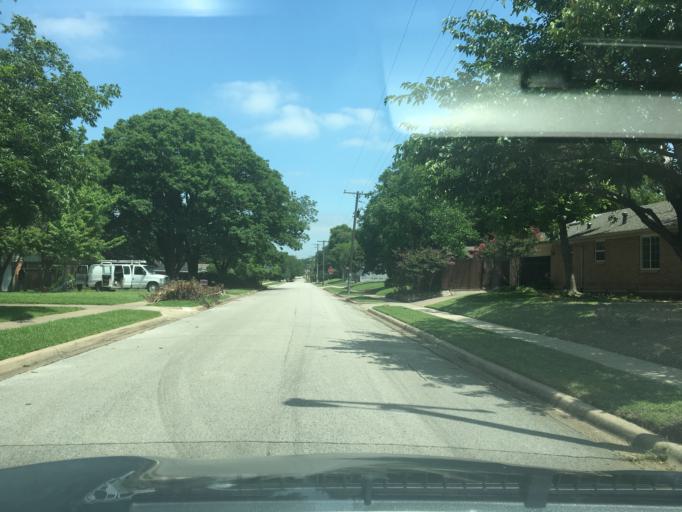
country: US
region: Texas
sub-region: Dallas County
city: Richardson
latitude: 32.9465
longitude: -96.7520
